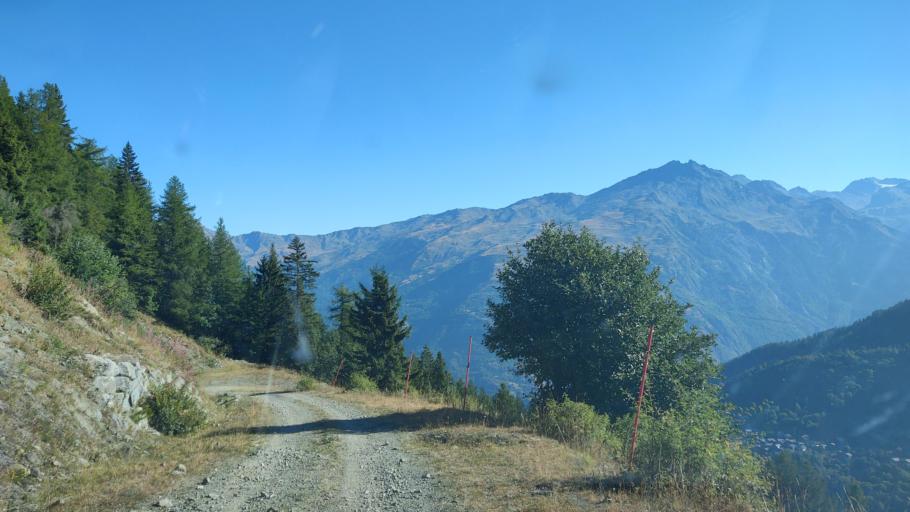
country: FR
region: Rhone-Alpes
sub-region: Departement de la Savoie
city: Saint-Michel-de-Maurienne
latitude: 45.1823
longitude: 6.4659
